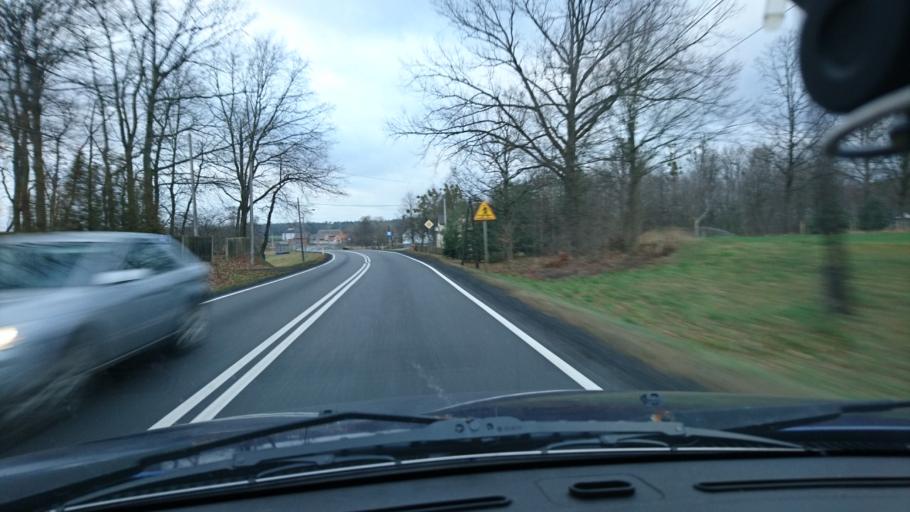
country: PL
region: Opole Voivodeship
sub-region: Powiat oleski
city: Olesno
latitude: 50.9117
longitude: 18.3537
